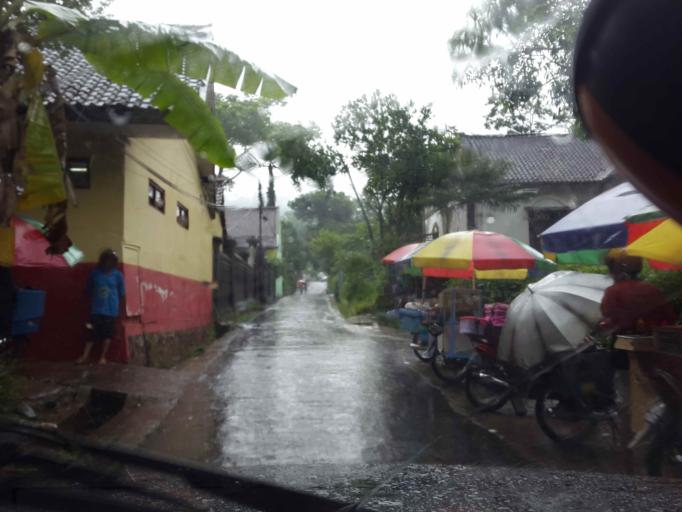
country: ID
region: Central Java
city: Salatiga
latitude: -7.3007
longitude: 110.4855
